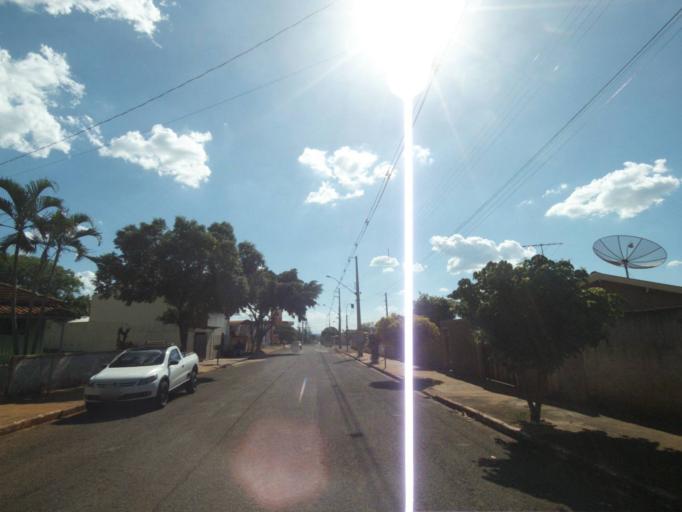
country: BR
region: Parana
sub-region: Sertanopolis
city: Sertanopolis
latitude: -23.0418
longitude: -50.8167
